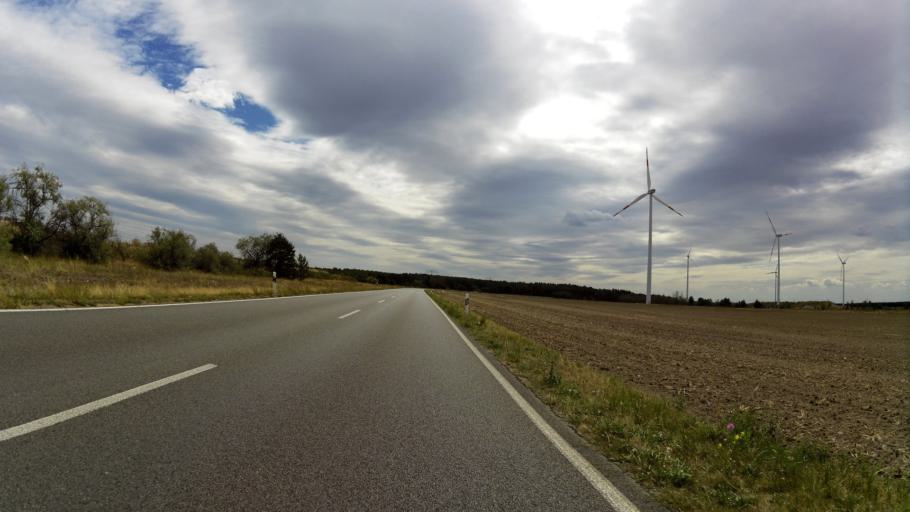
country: DE
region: Brandenburg
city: Heinersbruck
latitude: 51.7815
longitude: 14.4735
